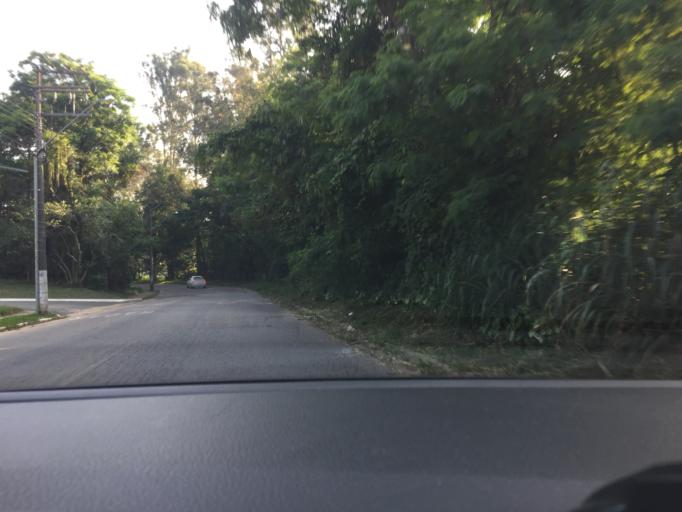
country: BR
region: Sao Paulo
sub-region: Valinhos
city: Valinhos
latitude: -23.0076
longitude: -47.0091
